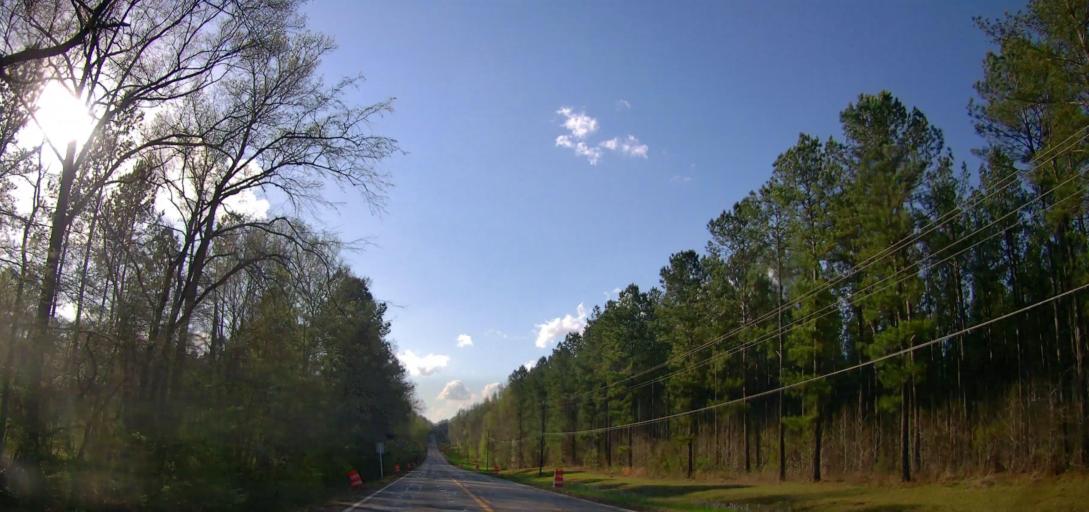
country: US
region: Georgia
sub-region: Putnam County
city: Eatonton
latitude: 33.1722
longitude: -83.3933
